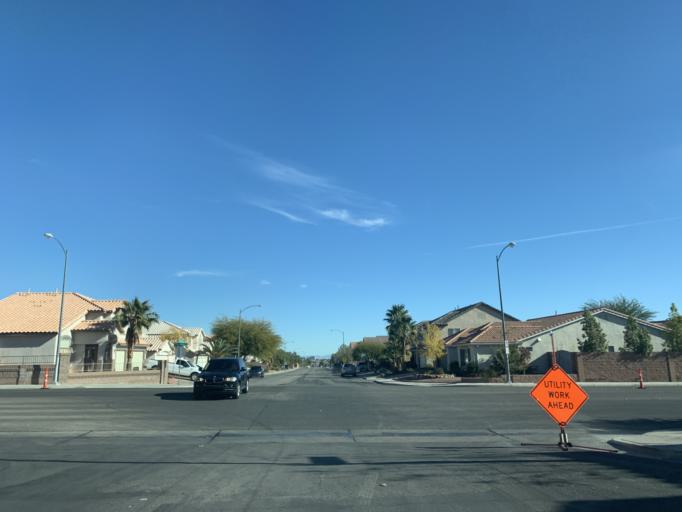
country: US
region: Nevada
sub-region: Clark County
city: Summerlin South
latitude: 36.1243
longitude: -115.3065
